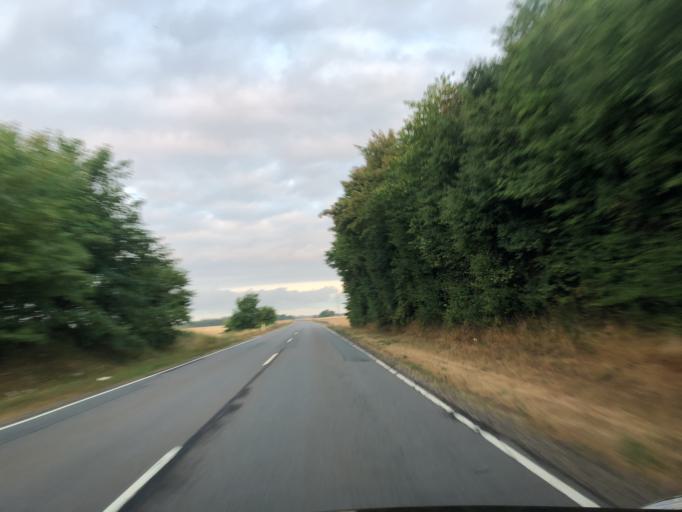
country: DK
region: Zealand
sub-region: Soro Kommune
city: Dianalund
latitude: 55.4625
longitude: 11.4589
